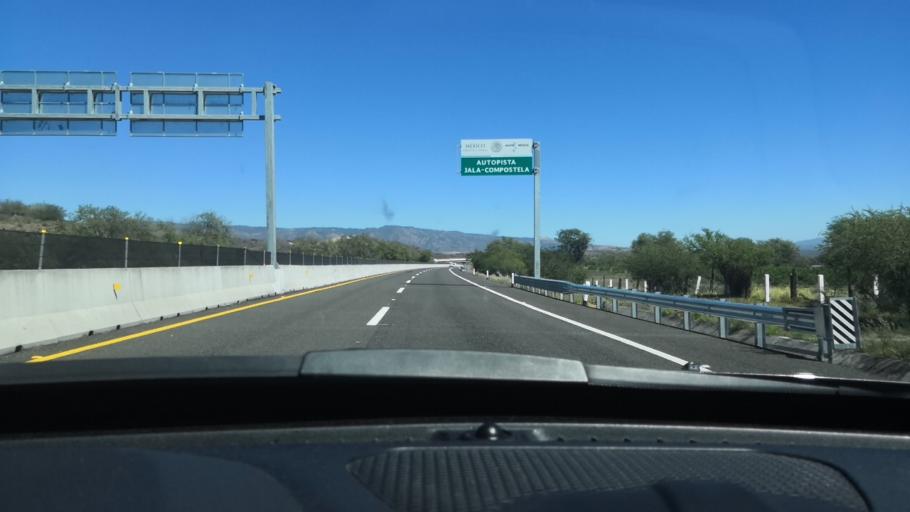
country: MX
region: Nayarit
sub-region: Ahuacatlan
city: Ahuacatlan
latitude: 21.0650
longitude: -104.4987
